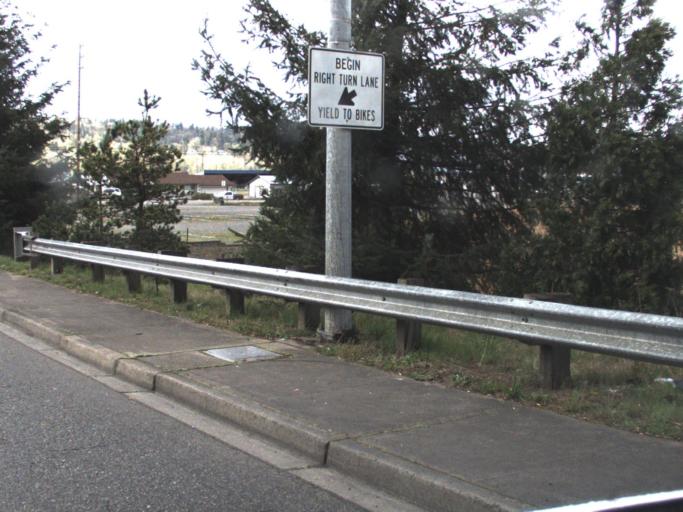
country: US
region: Washington
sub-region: King County
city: Pacific
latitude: 47.2332
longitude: -122.2539
